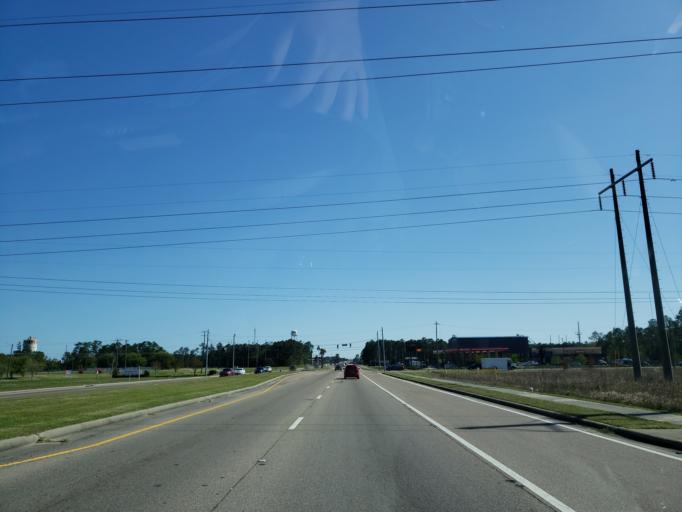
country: US
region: Mississippi
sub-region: Harrison County
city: West Gulfport
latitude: 30.4411
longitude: -89.0313
